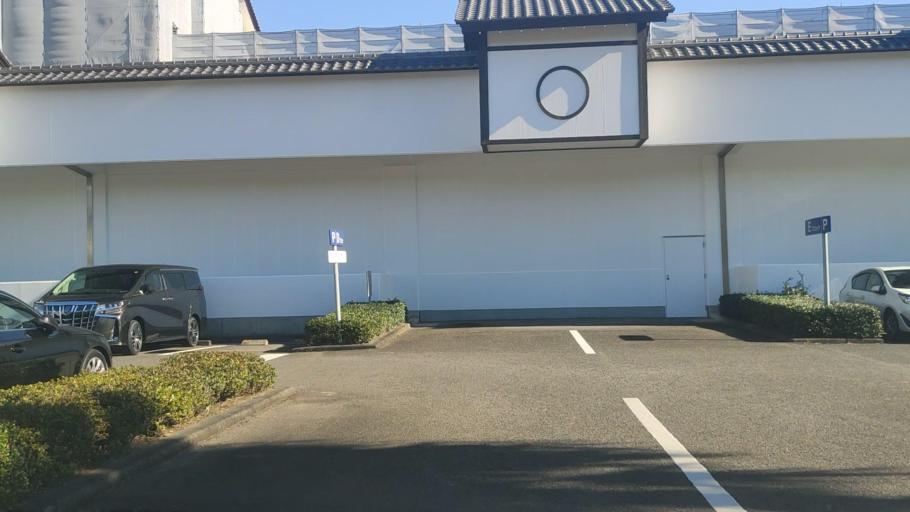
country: JP
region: Miyazaki
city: Miyazaki-shi
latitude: 31.9583
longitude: 131.4691
